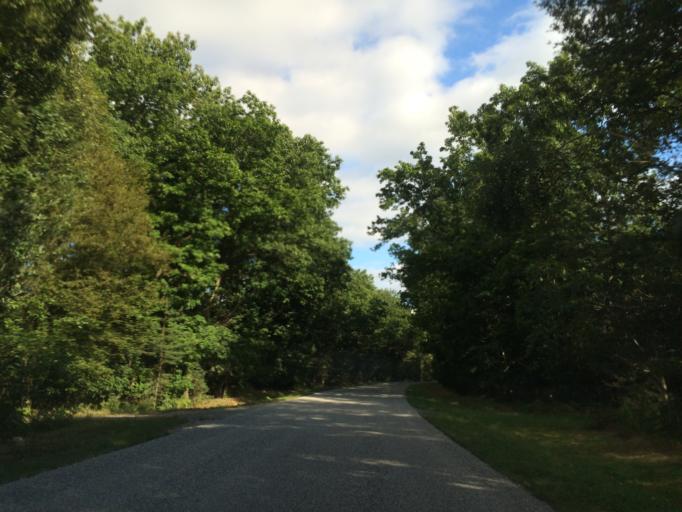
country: FR
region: Alsace
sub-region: Departement du Bas-Rhin
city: Soufflenheim
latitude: 48.8519
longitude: 7.9448
